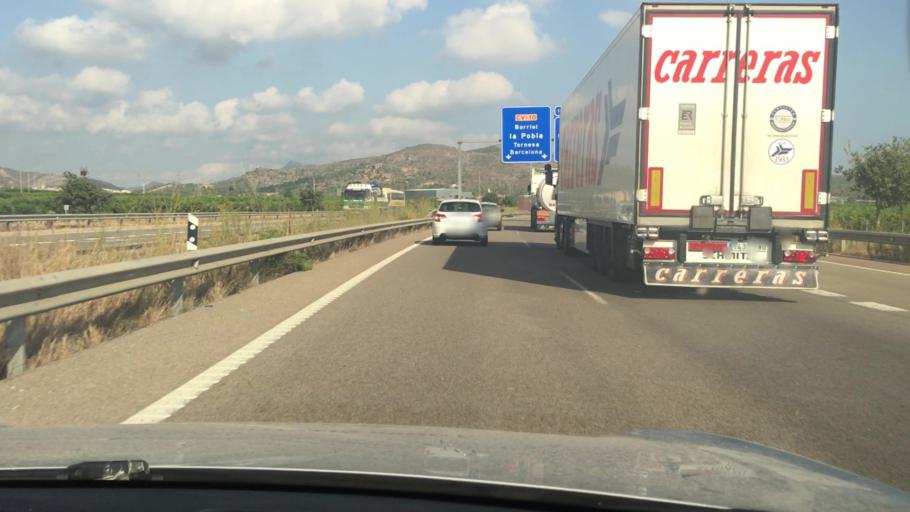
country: ES
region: Valencia
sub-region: Provincia de Castello
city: Borriol
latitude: 40.0102
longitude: -0.1096
